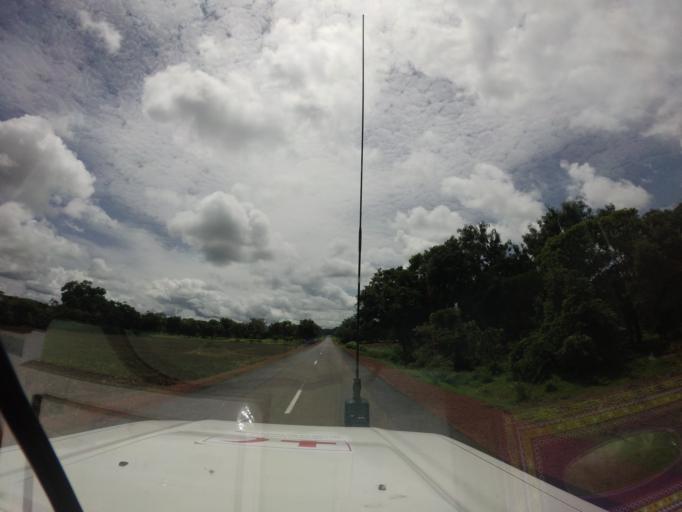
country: SL
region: Northern Province
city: Gberia Fotombu
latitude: 10.1238
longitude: -11.1594
